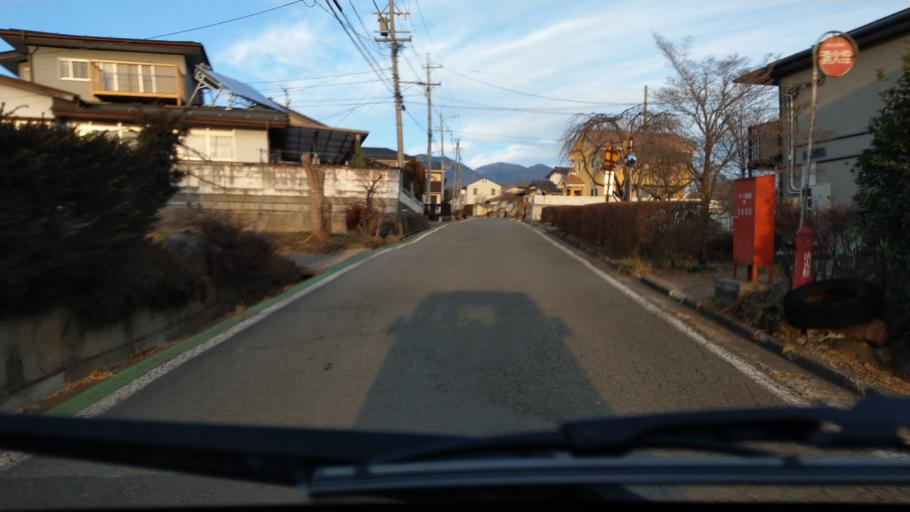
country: JP
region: Nagano
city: Komoro
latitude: 36.3449
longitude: 138.3897
